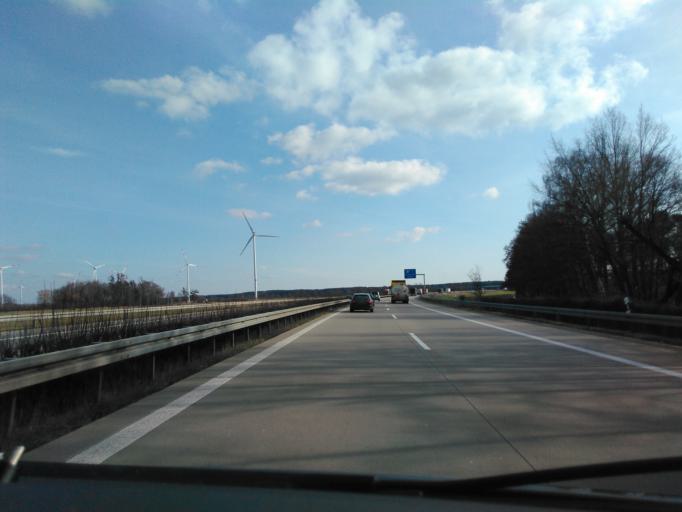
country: DE
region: Brandenburg
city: Kasel-Golzig
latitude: 51.9676
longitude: 13.7594
